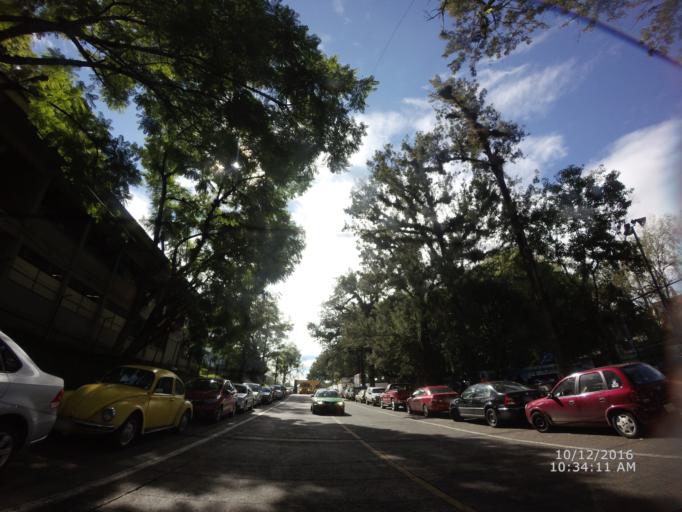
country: TR
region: Sivas
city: Karayun
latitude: 39.6712
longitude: 37.2558
